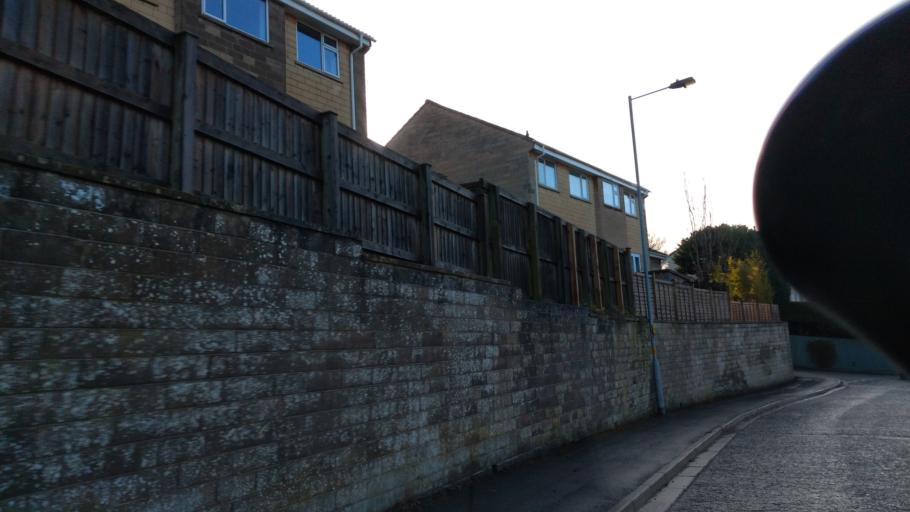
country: GB
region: England
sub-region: Wiltshire
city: Bradford-on-Avon
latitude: 51.3480
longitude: -2.2424
